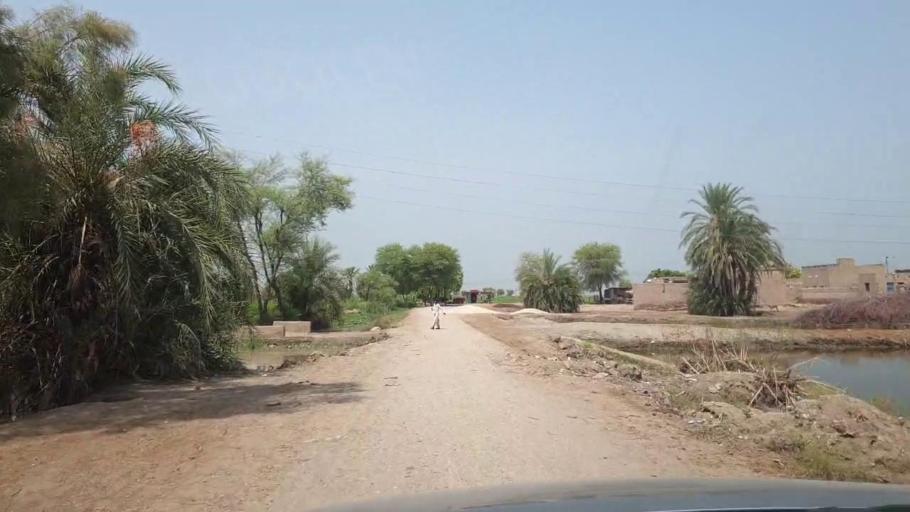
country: PK
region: Sindh
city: Madeji
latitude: 27.8093
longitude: 68.5192
